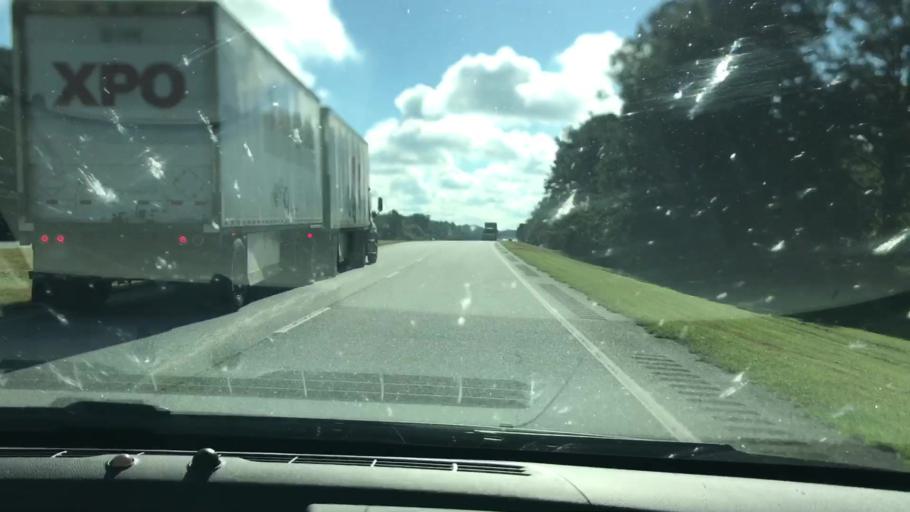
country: US
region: Georgia
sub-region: Worth County
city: Sylvester
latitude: 31.5544
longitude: -83.9885
